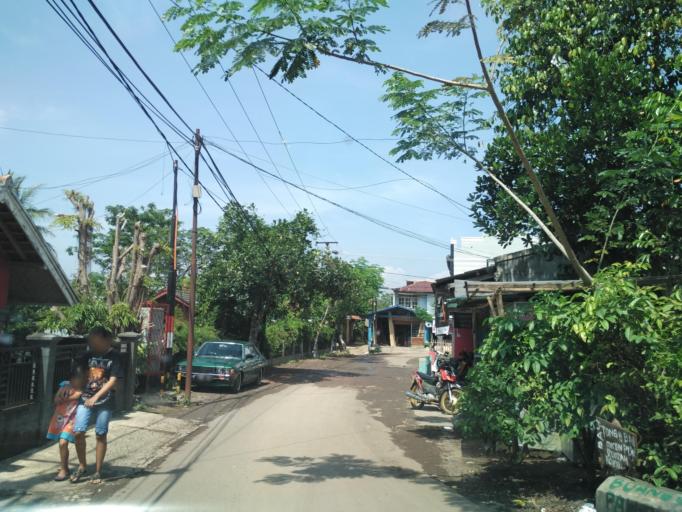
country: ID
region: West Java
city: Ciranjang-hilir
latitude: -6.8155
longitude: 107.1242
